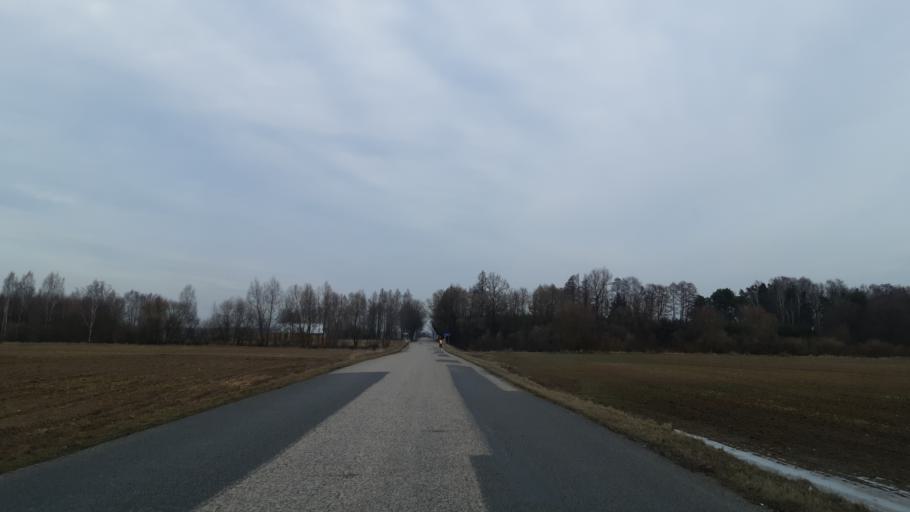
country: LT
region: Marijampoles apskritis
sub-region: Marijampole Municipality
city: Marijampole
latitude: 54.7119
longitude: 23.3170
